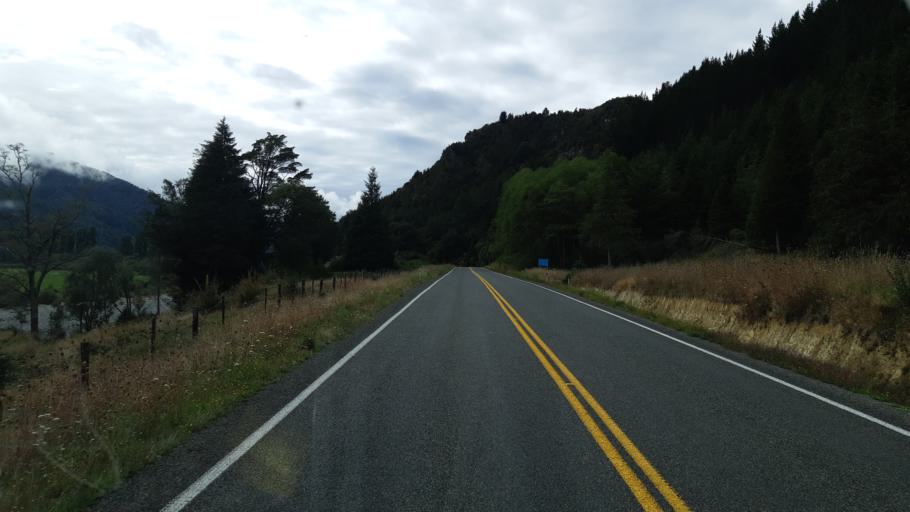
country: NZ
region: West Coast
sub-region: Buller District
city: Westport
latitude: -41.7817
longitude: 172.2635
